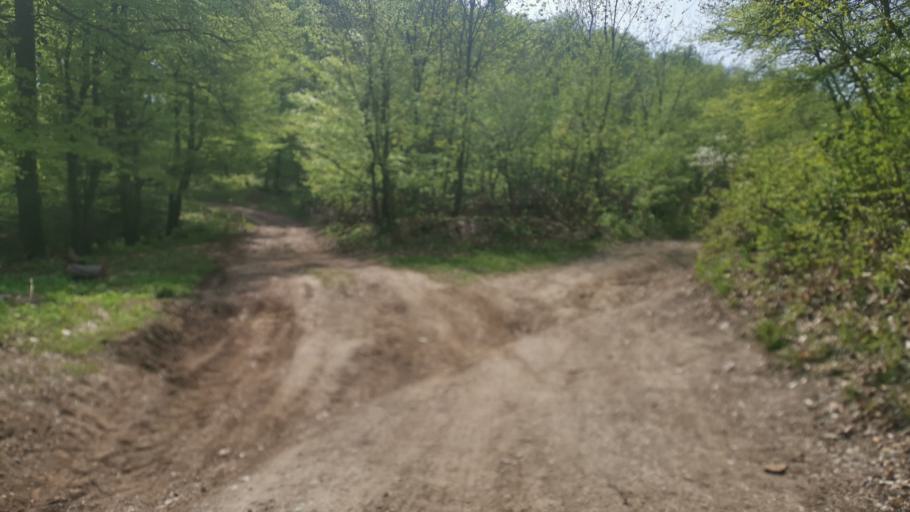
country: SK
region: Trnavsky
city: Smolenice
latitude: 48.5347
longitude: 17.4253
